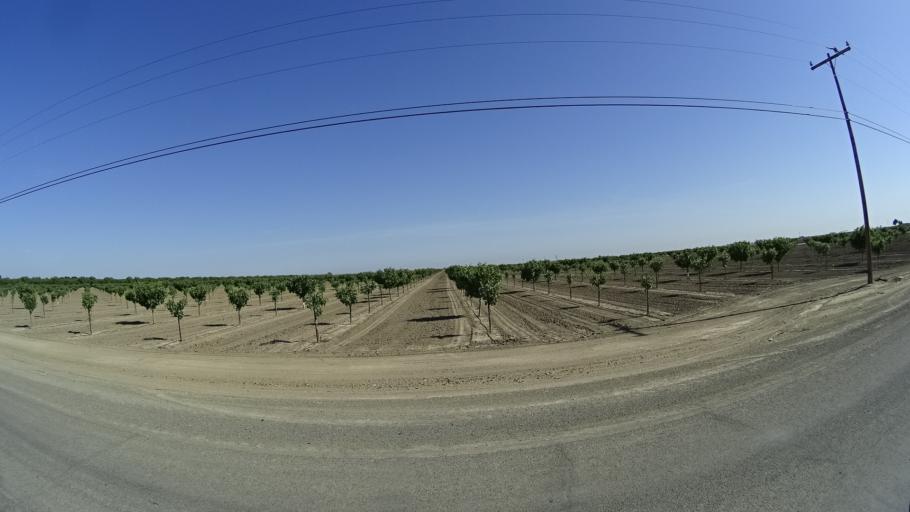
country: US
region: California
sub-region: Kings County
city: Home Garden
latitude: 36.2550
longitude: -119.5538
